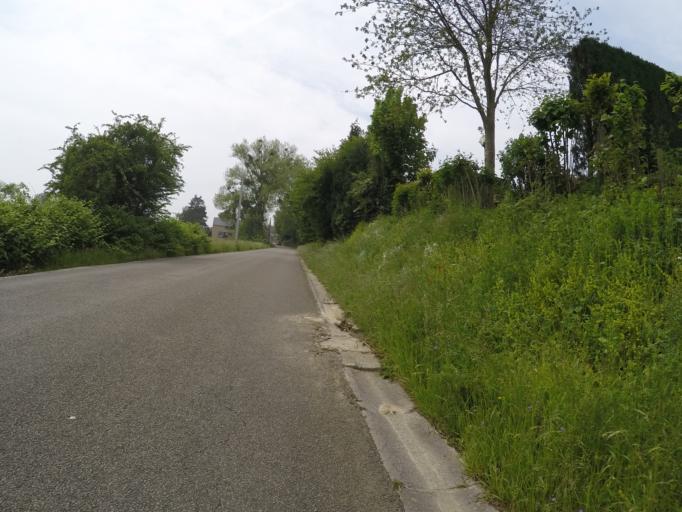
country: BE
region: Wallonia
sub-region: Province de Namur
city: Assesse
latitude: 50.3351
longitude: 4.9949
